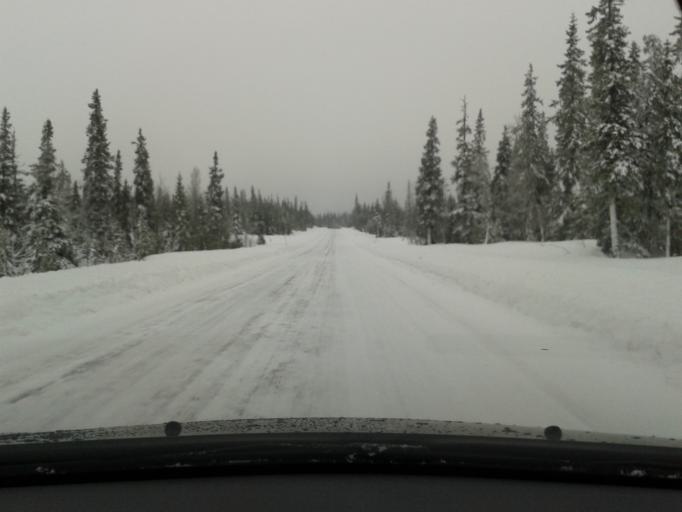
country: SE
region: Vaesterbotten
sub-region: Vilhelmina Kommun
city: Sjoberg
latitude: 65.0935
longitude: 15.8705
